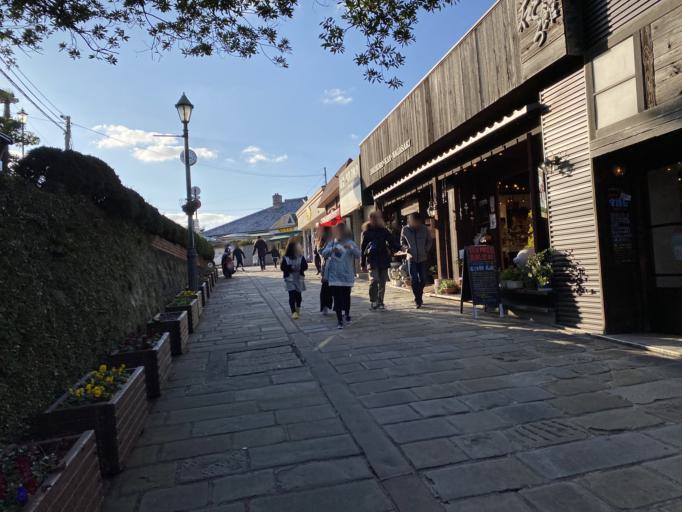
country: JP
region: Nagasaki
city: Nagasaki-shi
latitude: 32.7348
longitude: 129.8691
